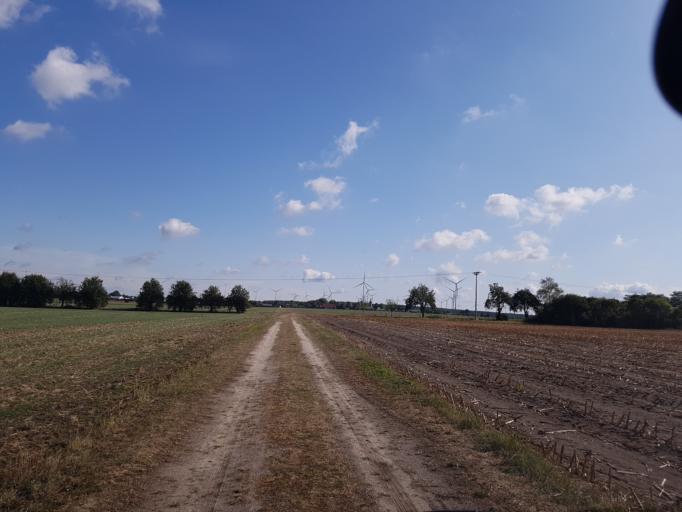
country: DE
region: Brandenburg
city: Finsterwalde
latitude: 51.6243
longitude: 13.7536
